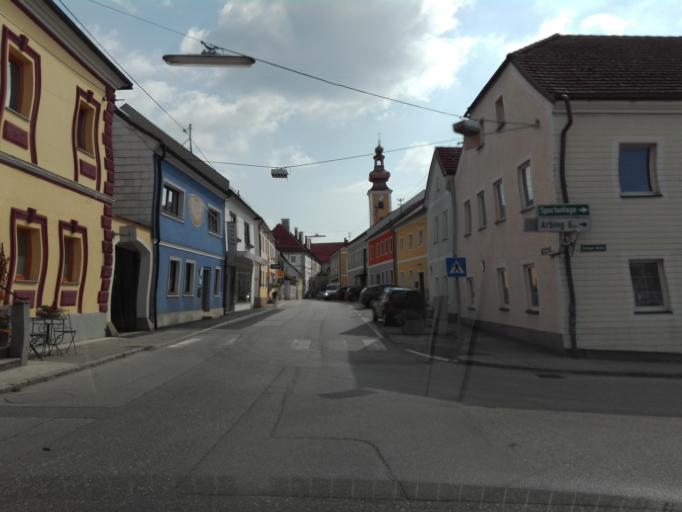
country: AT
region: Upper Austria
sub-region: Politischer Bezirk Perg
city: Perg
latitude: 48.2669
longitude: 14.7119
